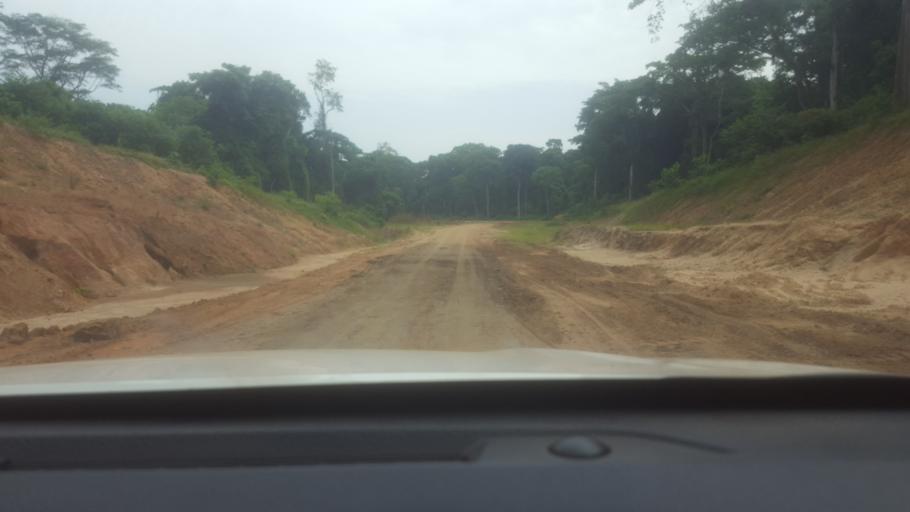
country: ET
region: Southern Nations, Nationalities, and People's Region
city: Tippi
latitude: 7.5082
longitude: 35.0057
